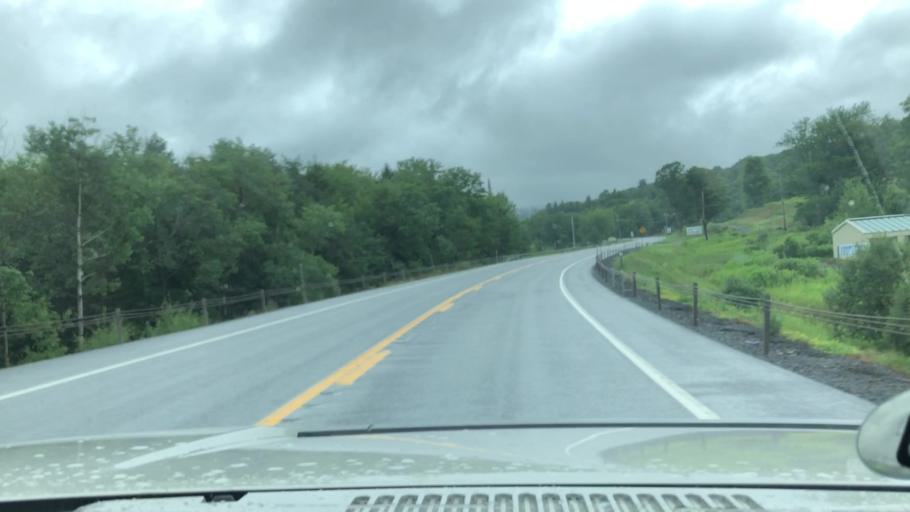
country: US
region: New York
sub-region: Greene County
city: Cairo
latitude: 42.3041
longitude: -74.2158
